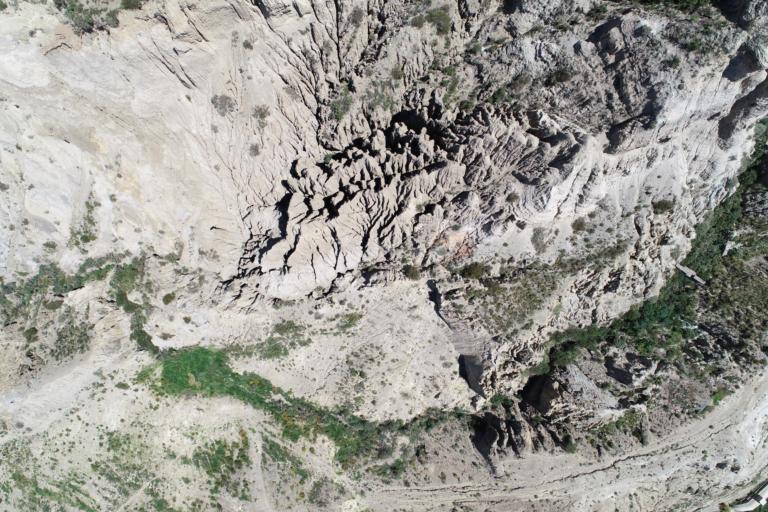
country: BO
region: La Paz
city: La Paz
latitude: -16.5157
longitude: -68.1005
